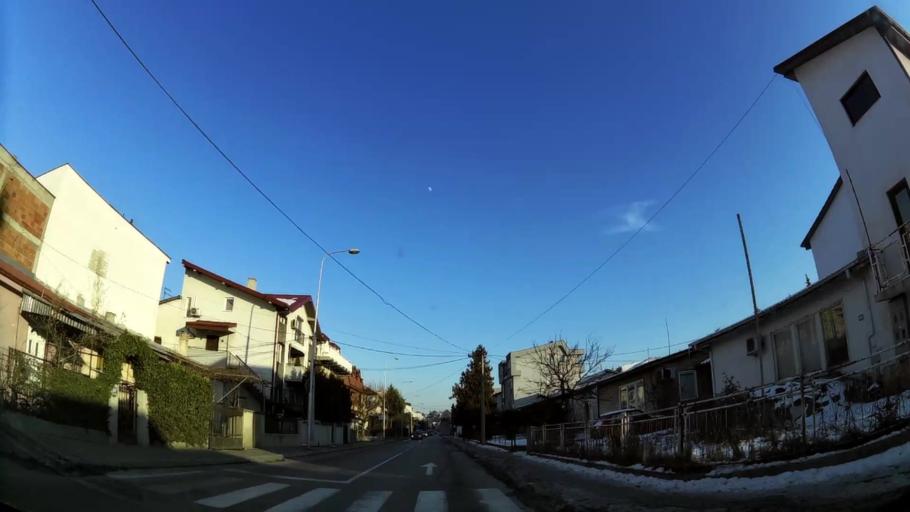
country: MK
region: Karpos
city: Skopje
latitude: 41.9942
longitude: 21.3994
